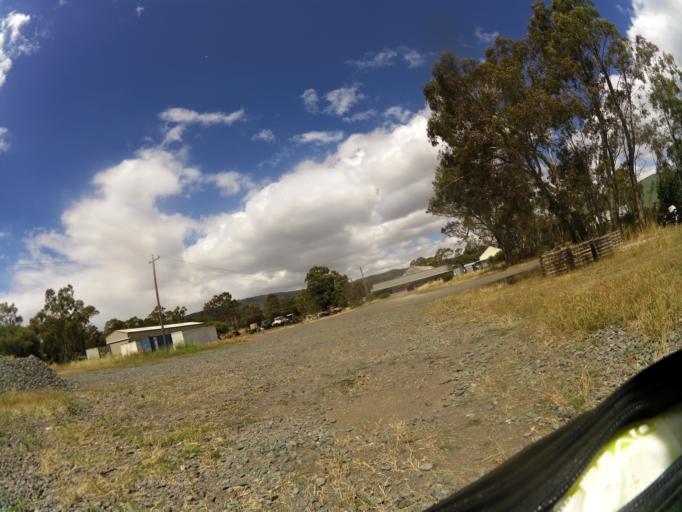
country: AU
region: Victoria
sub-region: Mount Alexander
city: Castlemaine
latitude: -37.0035
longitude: 144.2538
